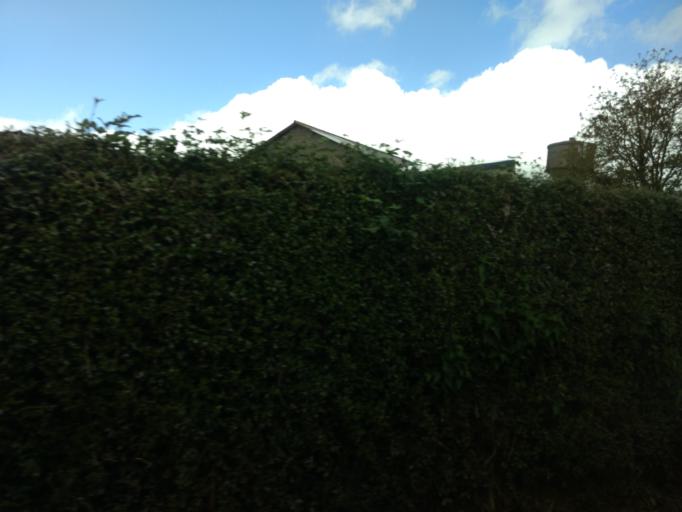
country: FR
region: Midi-Pyrenees
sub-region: Departement de l'Aveyron
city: Cassagnes-Begonhes
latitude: 44.1118
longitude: 2.6185
